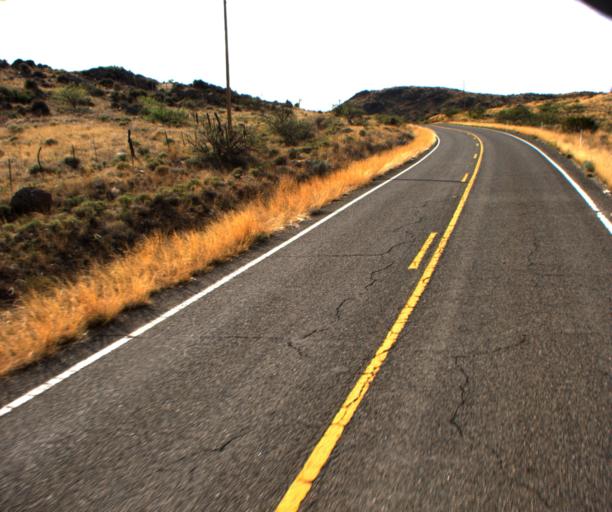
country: US
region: Arizona
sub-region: Cochise County
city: Willcox
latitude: 32.1658
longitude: -109.5791
